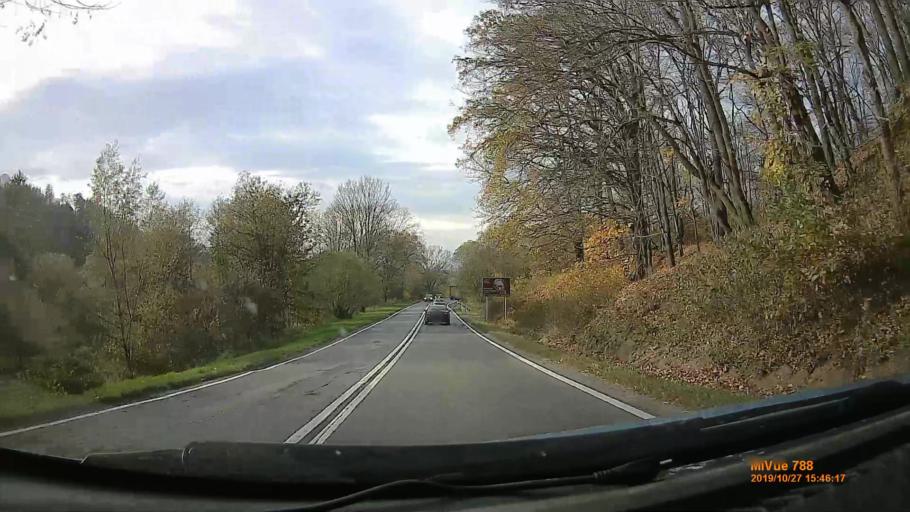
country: PL
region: Lower Silesian Voivodeship
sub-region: Powiat klodzki
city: Bozkow
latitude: 50.4809
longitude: 16.5865
